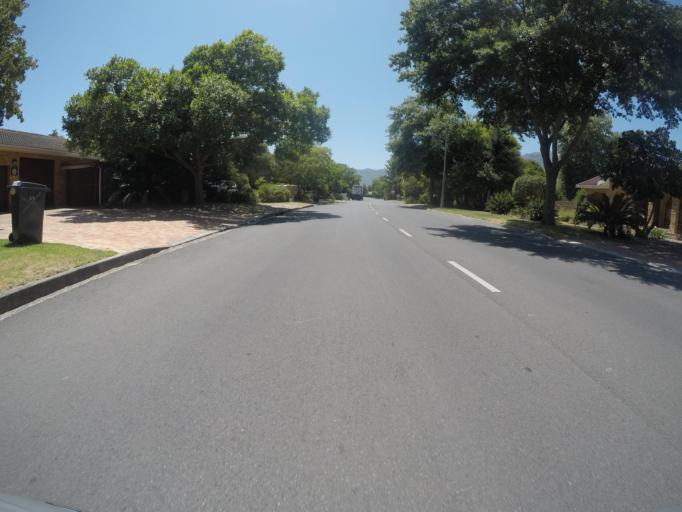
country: ZA
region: Western Cape
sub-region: Cape Winelands District Municipality
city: Stellenbosch
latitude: -33.9453
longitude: 18.8481
